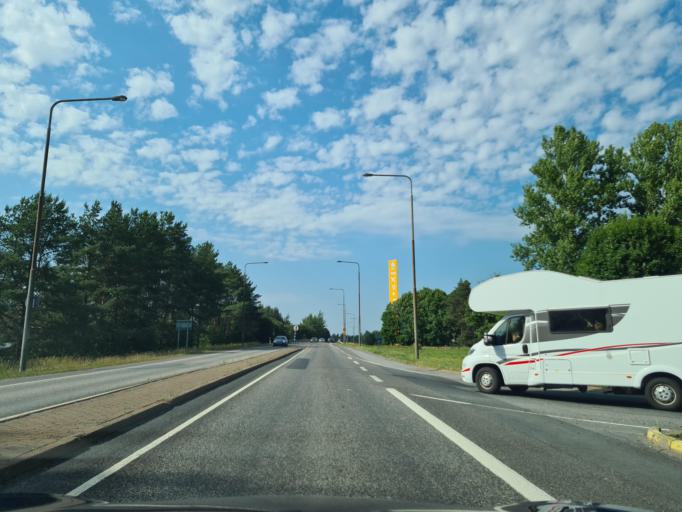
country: FI
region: Satakunta
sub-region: Pori
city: Pori
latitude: 61.4853
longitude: 21.7518
